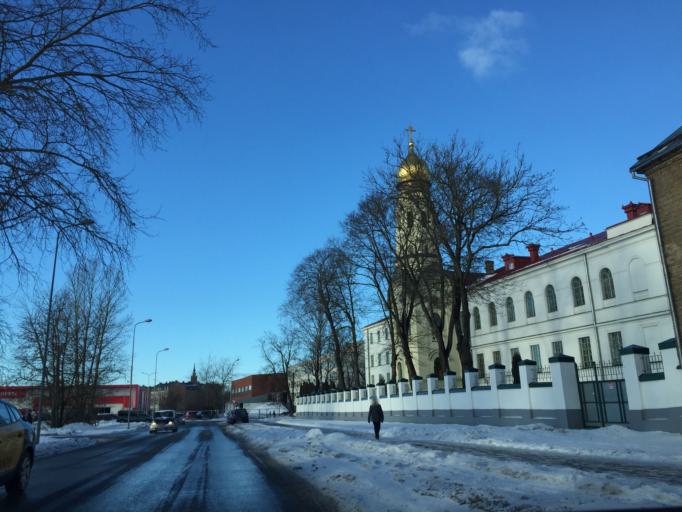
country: LV
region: Riga
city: Riga
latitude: 56.9369
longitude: 24.1404
